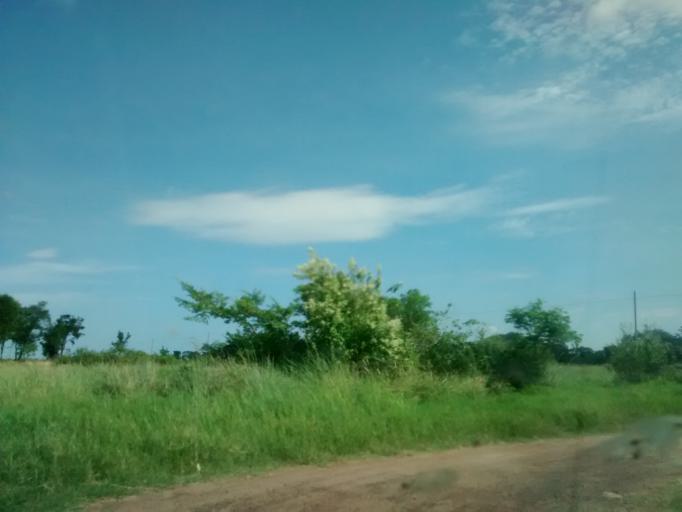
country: AR
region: Chaco
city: Fontana
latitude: -27.4093
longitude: -58.9721
